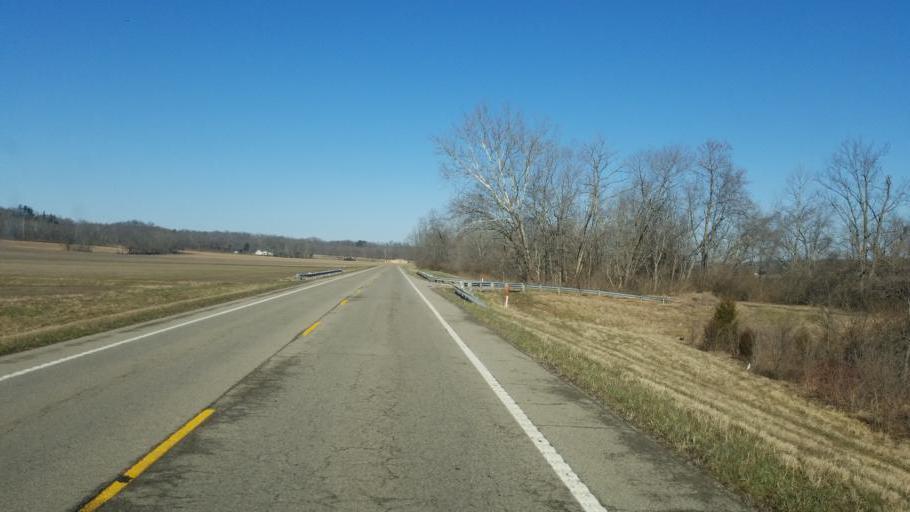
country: US
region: Ohio
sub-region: Highland County
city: Greenfield
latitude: 39.2222
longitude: -83.3046
